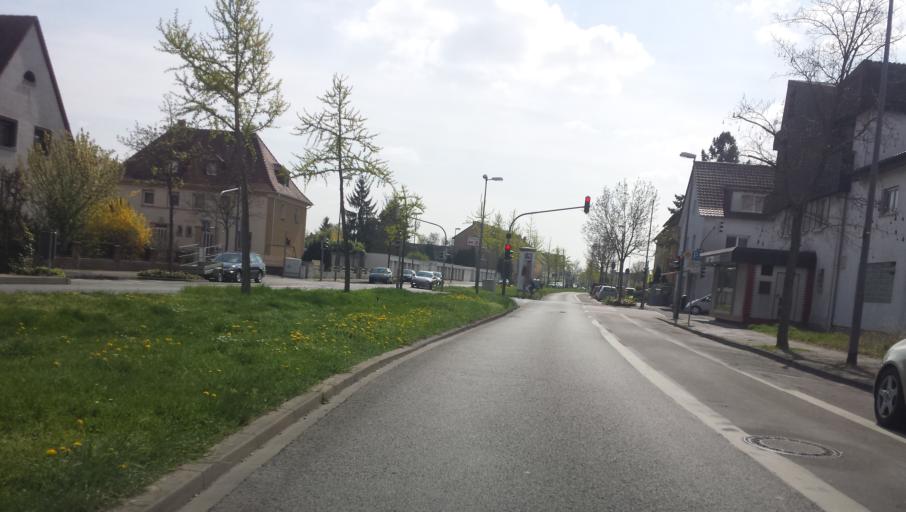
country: DE
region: Rheinland-Pfalz
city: Gartenstadt
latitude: 49.4608
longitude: 8.4017
